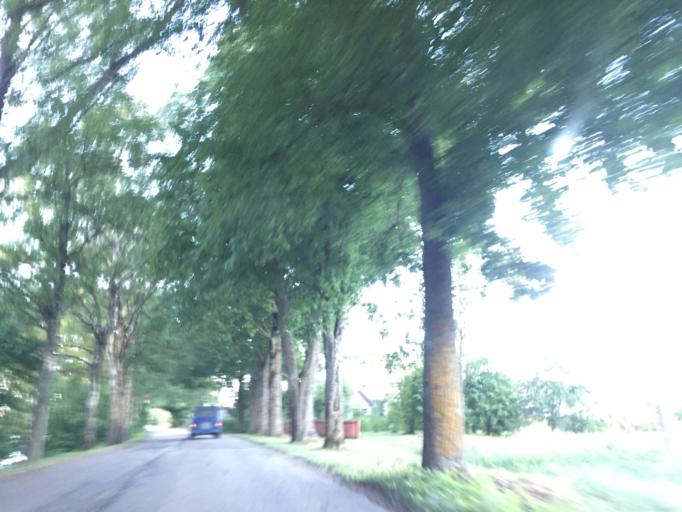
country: LV
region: Plavinu
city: Plavinas
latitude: 56.6097
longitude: 25.8130
